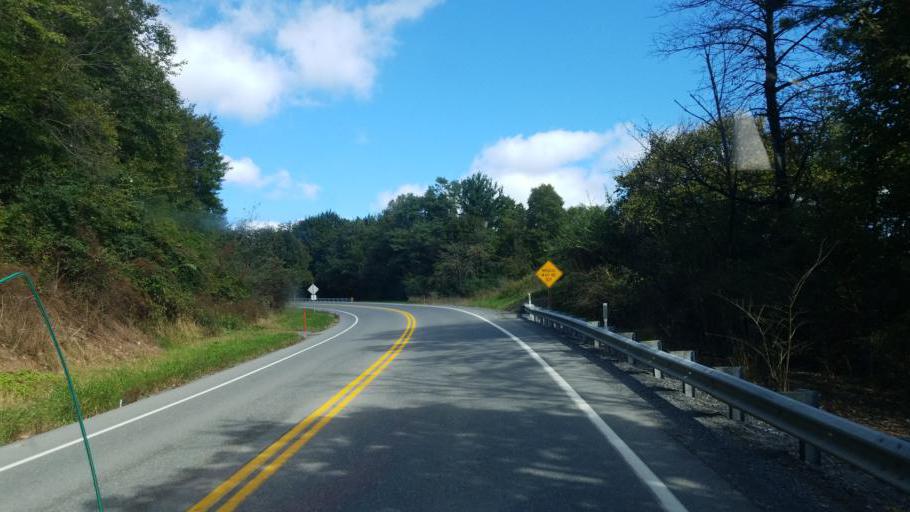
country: US
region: Pennsylvania
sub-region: Fulton County
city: McConnellsburg
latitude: 39.9361
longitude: -78.0159
